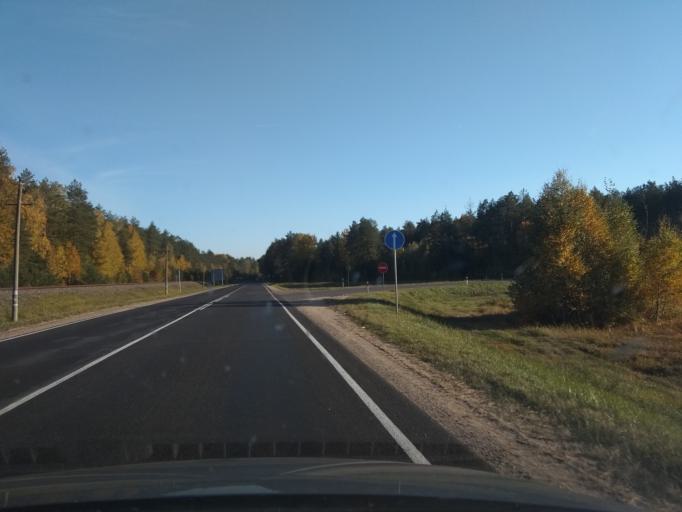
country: BY
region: Brest
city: Nyakhachava
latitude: 52.5734
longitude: 25.1145
